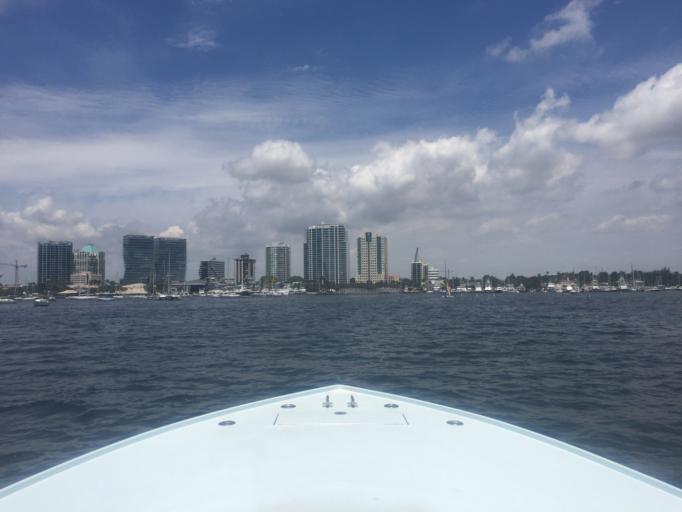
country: US
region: Florida
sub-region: Miami-Dade County
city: Coconut Grove
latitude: 25.7279
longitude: -80.2273
